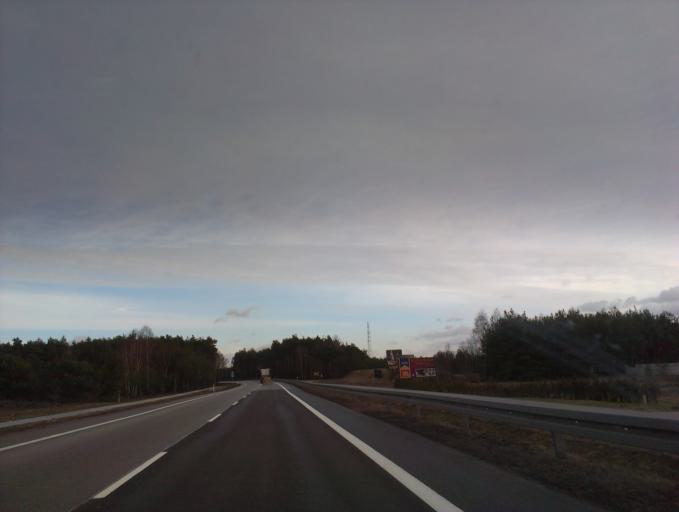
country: PL
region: Kujawsko-Pomorskie
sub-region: Powiat lipnowski
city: Skepe
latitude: 52.8757
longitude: 19.3487
